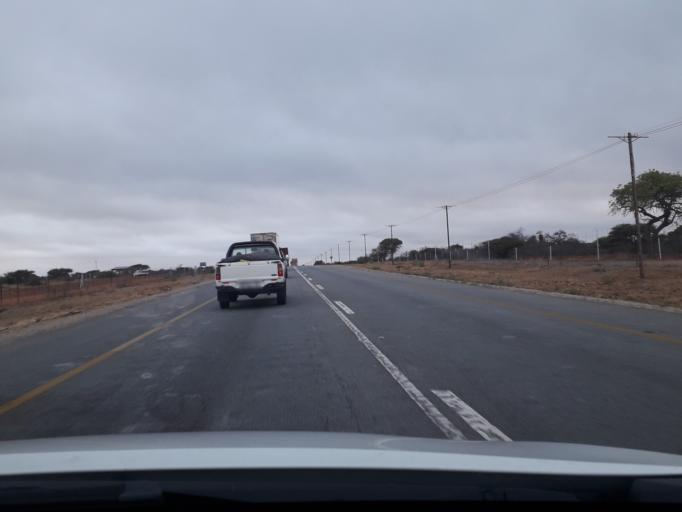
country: ZA
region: Limpopo
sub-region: Capricorn District Municipality
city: Mankoeng
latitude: -23.5854
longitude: 29.6659
